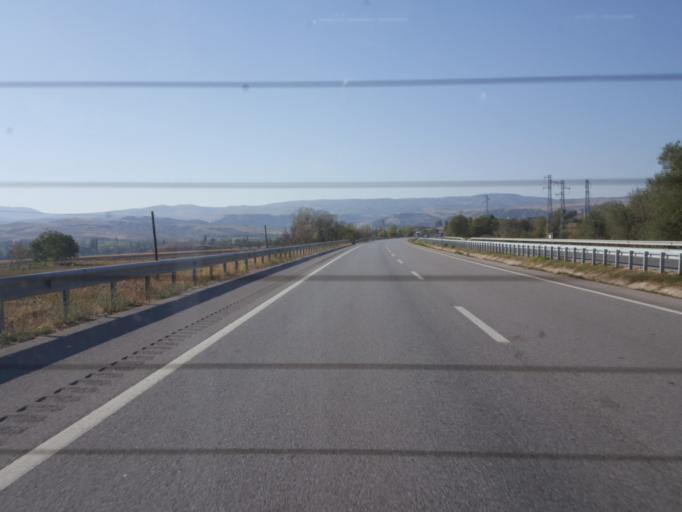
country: TR
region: Amasya
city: Saribugday
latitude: 40.7607
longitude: 35.4512
